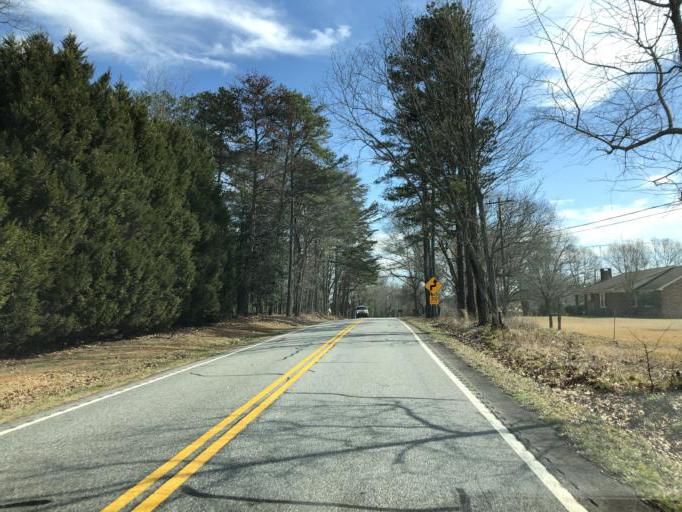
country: US
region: South Carolina
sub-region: Spartanburg County
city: Mayo
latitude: 35.0526
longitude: -81.9001
